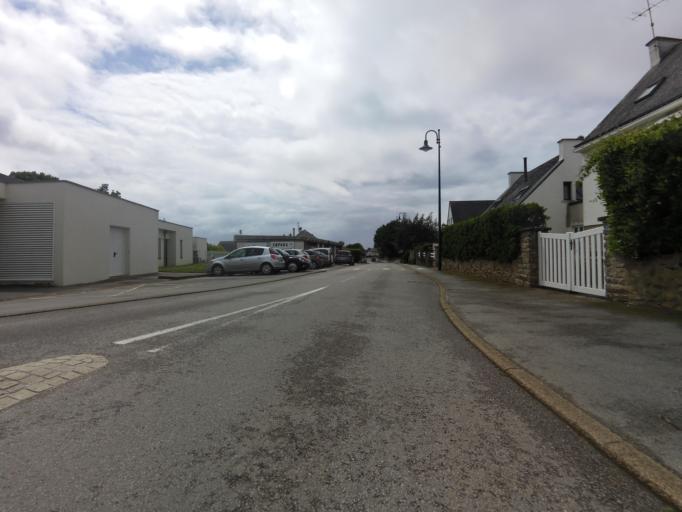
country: FR
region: Brittany
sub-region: Departement du Morbihan
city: Baden
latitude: 47.6174
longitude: -2.9201
